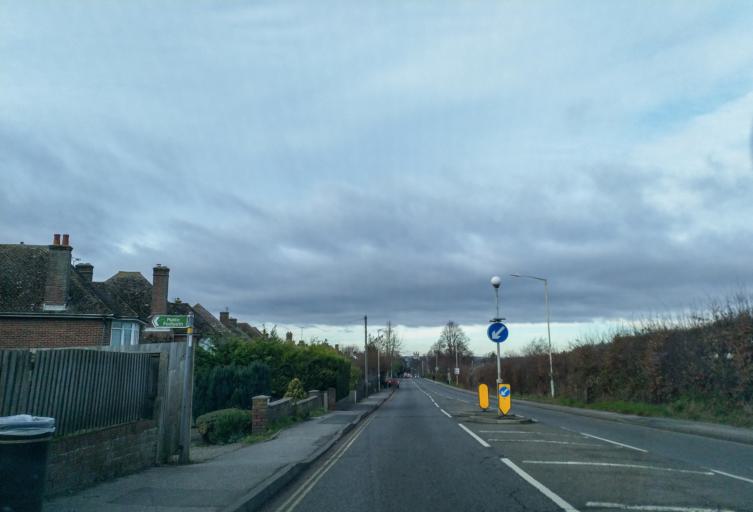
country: GB
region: England
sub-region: Kent
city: Canterbury
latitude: 51.2656
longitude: 1.0992
